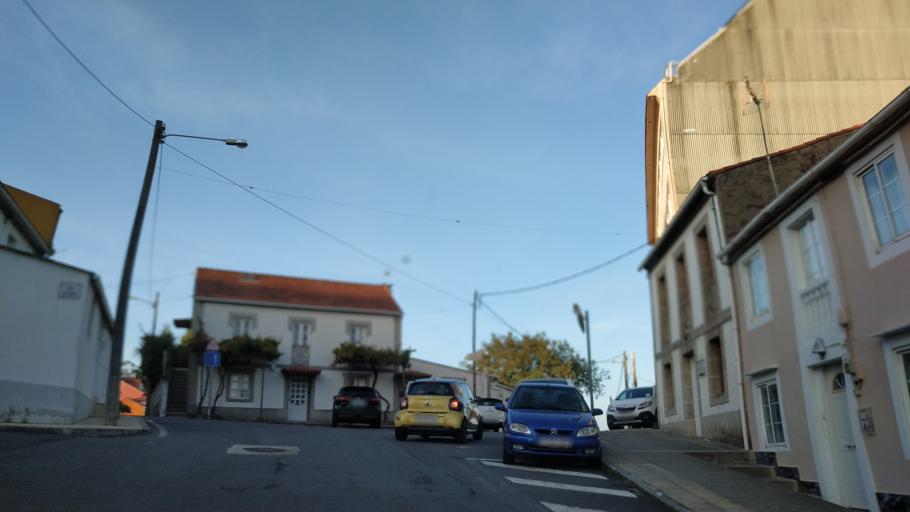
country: ES
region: Galicia
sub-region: Provincia da Coruna
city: Oleiros
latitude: 43.3511
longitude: -8.3459
